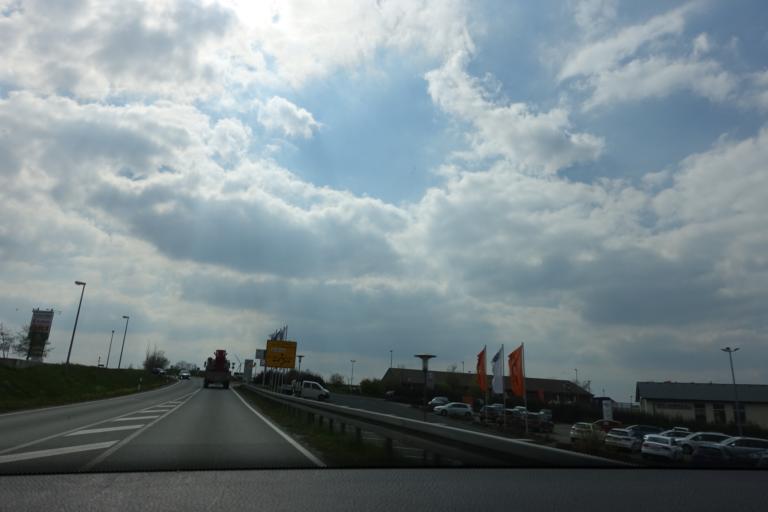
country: DE
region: Saxony
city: Gornau
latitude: 50.7582
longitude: 13.0533
